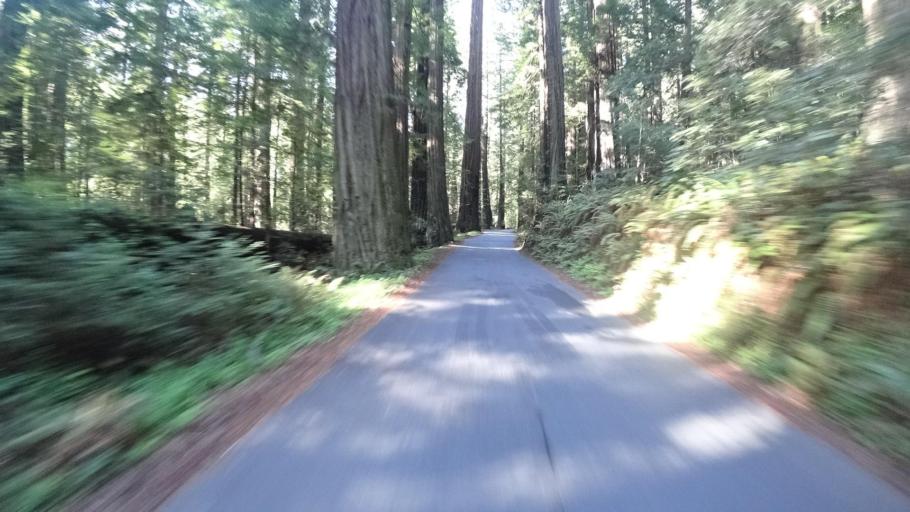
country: US
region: California
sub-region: Humboldt County
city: Rio Dell
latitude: 40.3463
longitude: -123.9331
